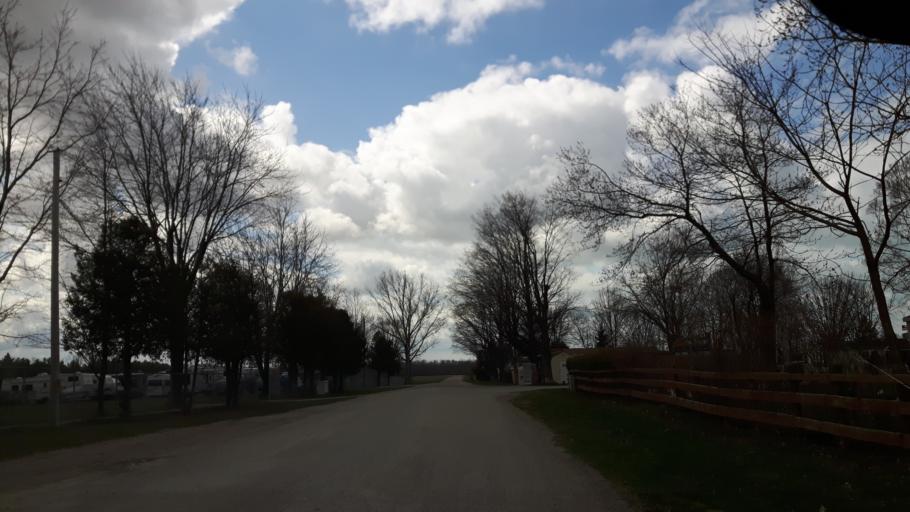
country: CA
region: Ontario
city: Bluewater
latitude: 43.5492
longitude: -81.7008
